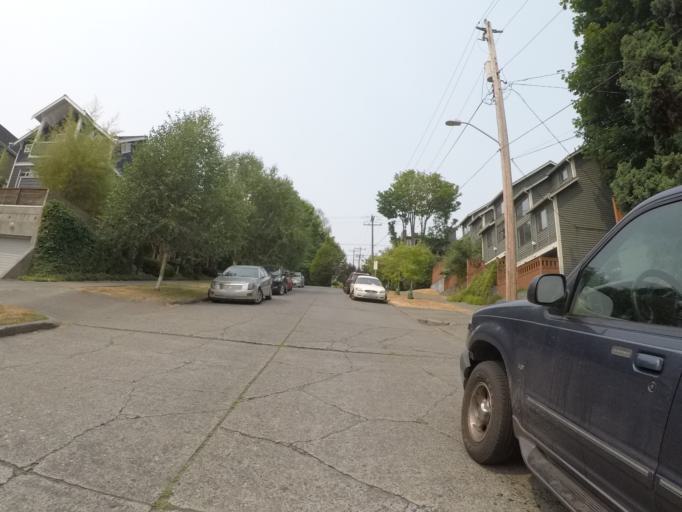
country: US
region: Washington
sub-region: King County
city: Seattle
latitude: 47.6202
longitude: -122.2991
